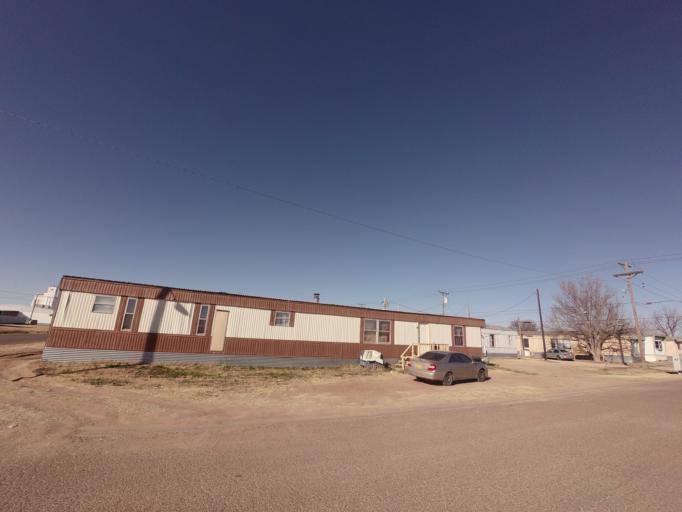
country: US
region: New Mexico
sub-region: Curry County
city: Clovis
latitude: 34.3998
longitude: -103.1914
